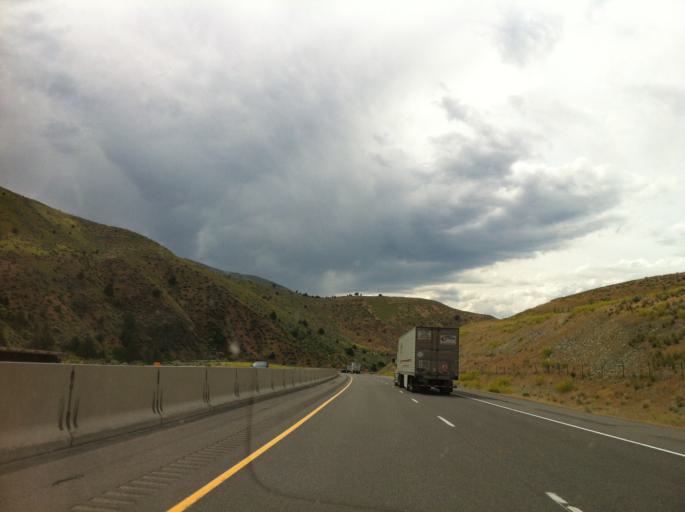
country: US
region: Idaho
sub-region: Washington County
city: Weiser
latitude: 44.4890
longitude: -117.3630
